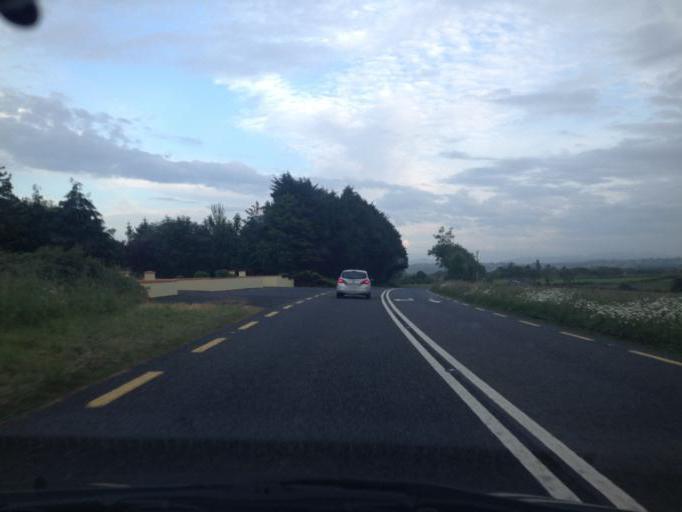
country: IE
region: Connaught
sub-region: Sligo
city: Sligo
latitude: 54.3514
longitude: -8.5071
